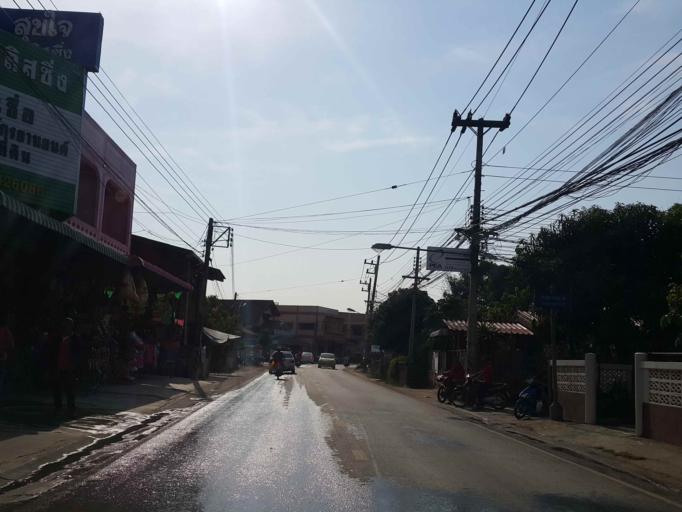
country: TH
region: Sukhothai
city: Thung Saliam
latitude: 17.3171
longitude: 99.5511
